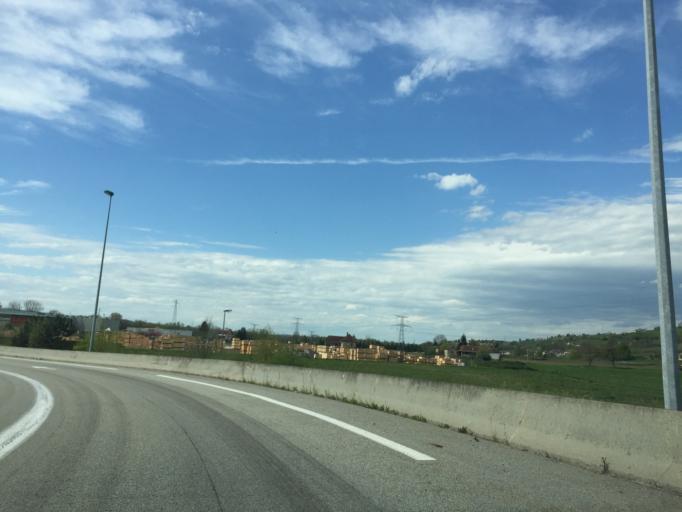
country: FR
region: Rhone-Alpes
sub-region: Departement de l'Isere
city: Romagnieu
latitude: 45.5729
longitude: 5.6617
